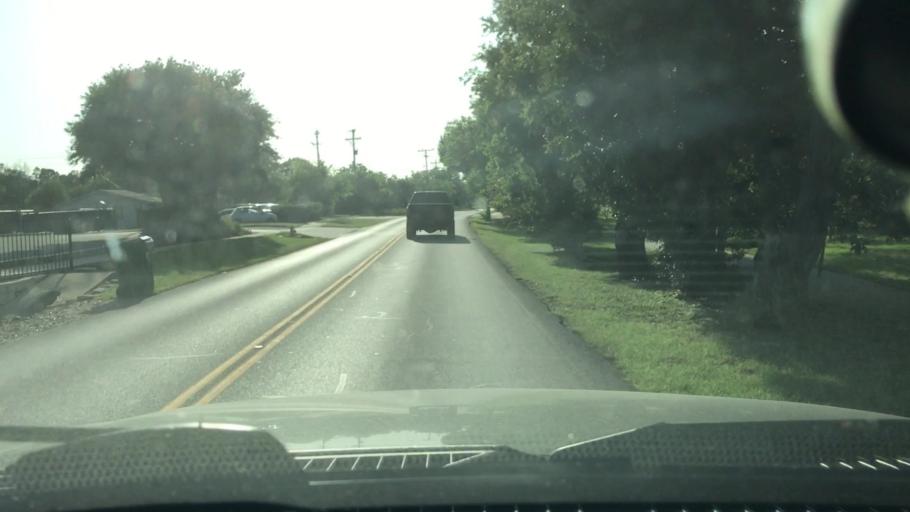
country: US
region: Texas
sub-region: Williamson County
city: Cedar Park
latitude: 30.5050
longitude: -97.8166
